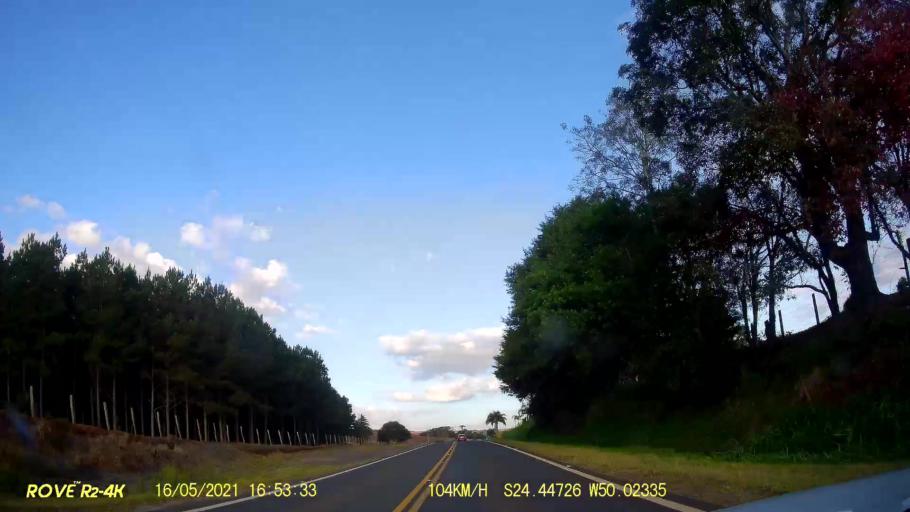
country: BR
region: Parana
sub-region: Pirai Do Sul
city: Pirai do Sul
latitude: -24.4467
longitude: -50.0239
